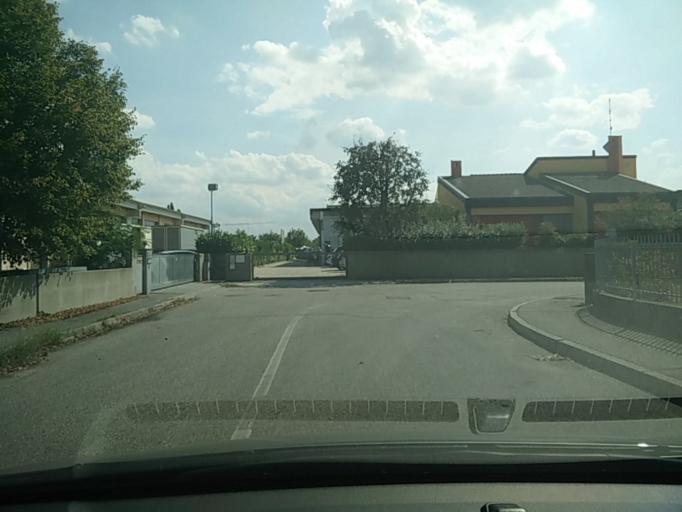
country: IT
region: Veneto
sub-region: Provincia di Treviso
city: Salvatronda
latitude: 45.6807
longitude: 11.9769
